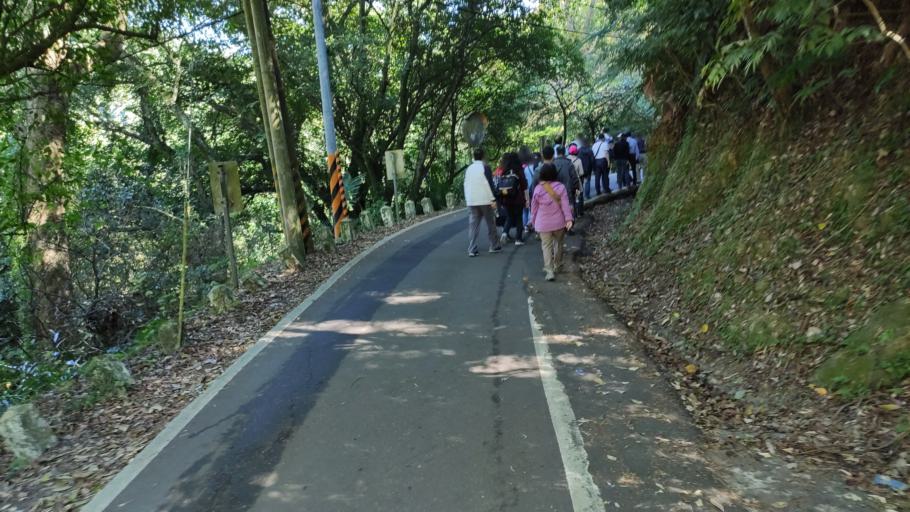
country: TW
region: Taiwan
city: Daxi
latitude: 24.8358
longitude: 121.3025
